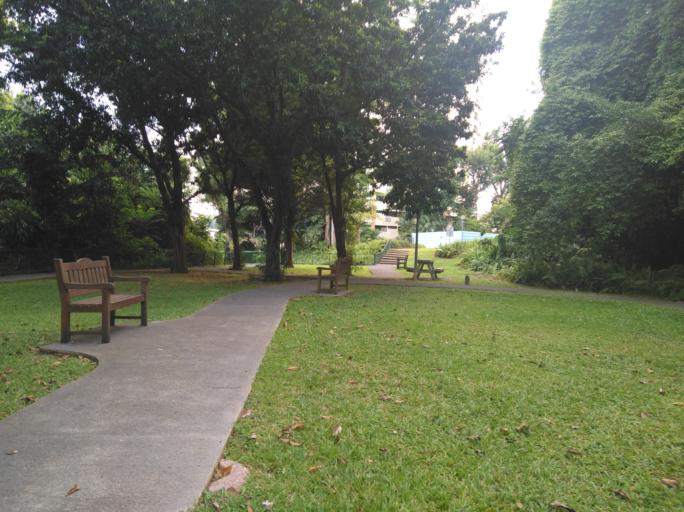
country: SG
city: Singapore
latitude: 1.2839
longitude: 103.8407
